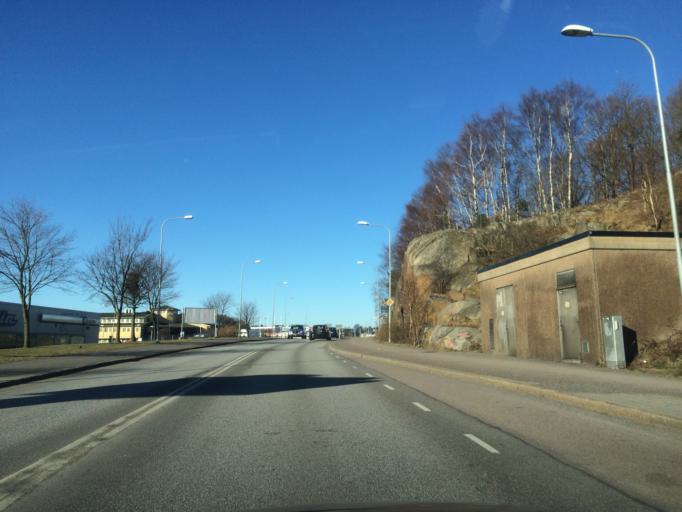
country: SE
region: Vaestra Goetaland
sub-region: Goteborg
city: Majorna
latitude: 57.6499
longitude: 11.9552
